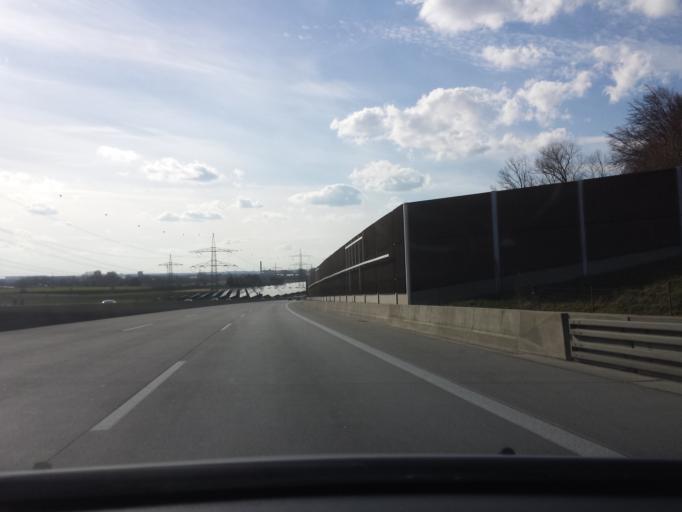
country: DE
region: Bavaria
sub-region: Swabia
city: Friedberg
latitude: 48.4016
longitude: 10.9738
